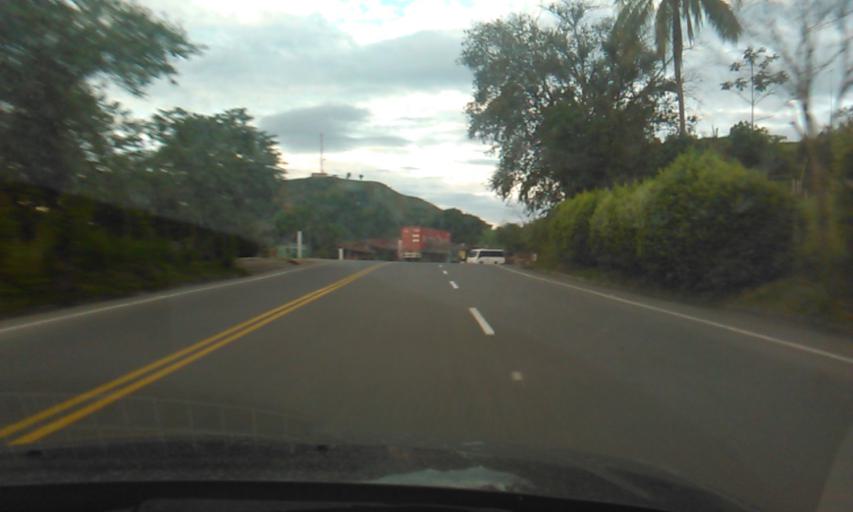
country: CO
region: Valle del Cauca
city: Caicedonia
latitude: 4.4089
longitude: -75.8895
